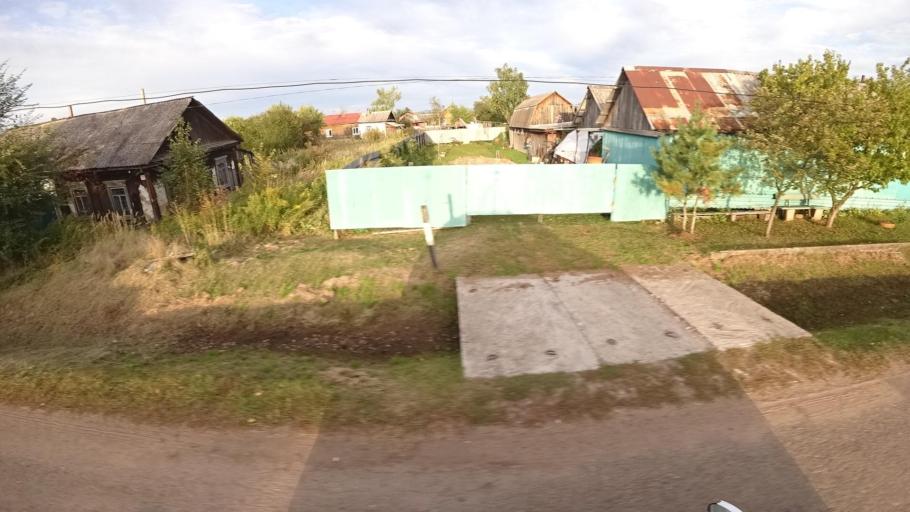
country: RU
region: Primorskiy
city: Yakovlevka
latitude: 44.4297
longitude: 133.4752
